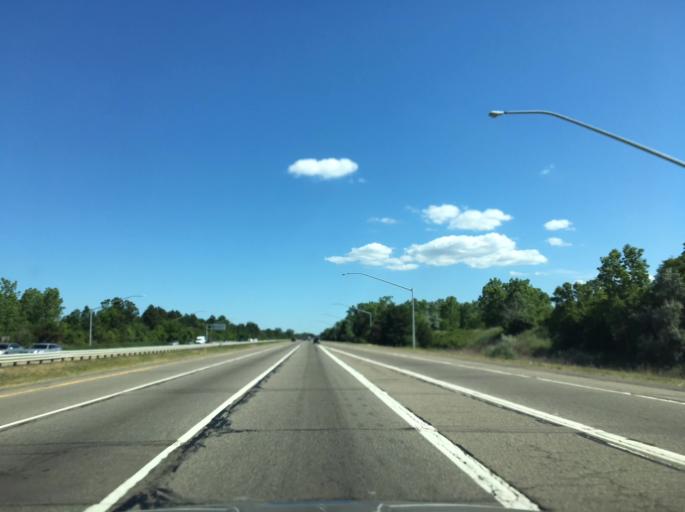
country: US
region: Michigan
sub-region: Oakland County
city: Clawson
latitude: 42.5674
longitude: -83.1588
